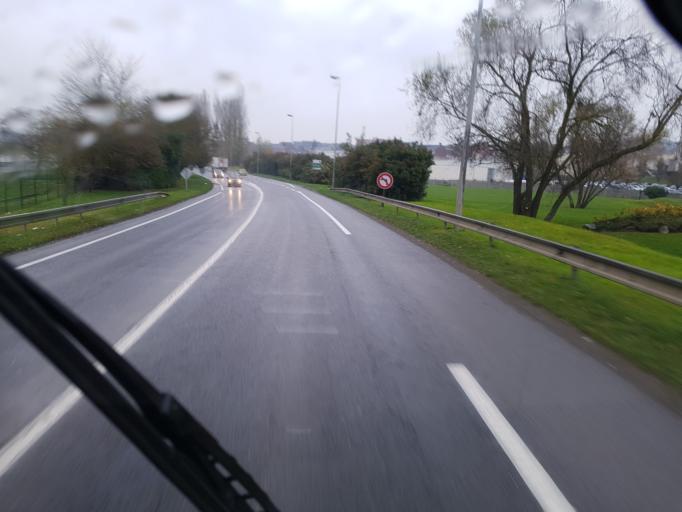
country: FR
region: Picardie
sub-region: Departement de l'Aisne
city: Saint-Quentin
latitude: 49.8395
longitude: 3.2836
